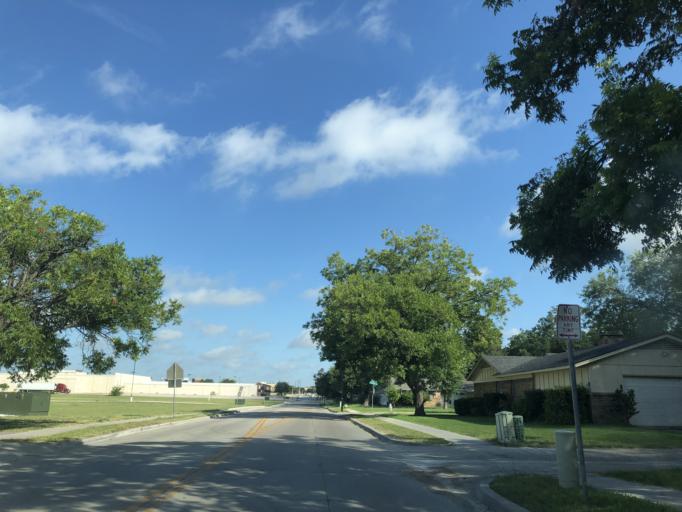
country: US
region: Texas
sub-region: Dallas County
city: Garland
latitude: 32.8558
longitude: -96.6415
